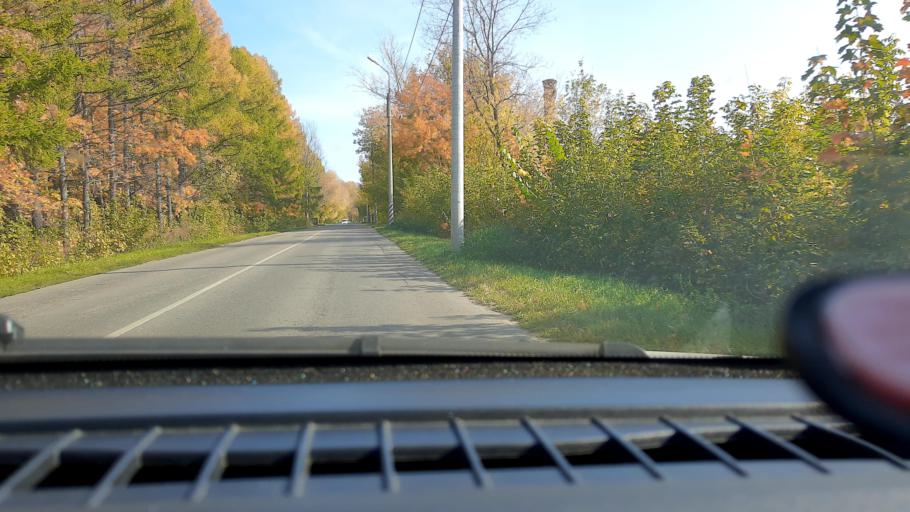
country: RU
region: Nizjnij Novgorod
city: Kstovo
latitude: 56.1570
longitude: 44.2546
